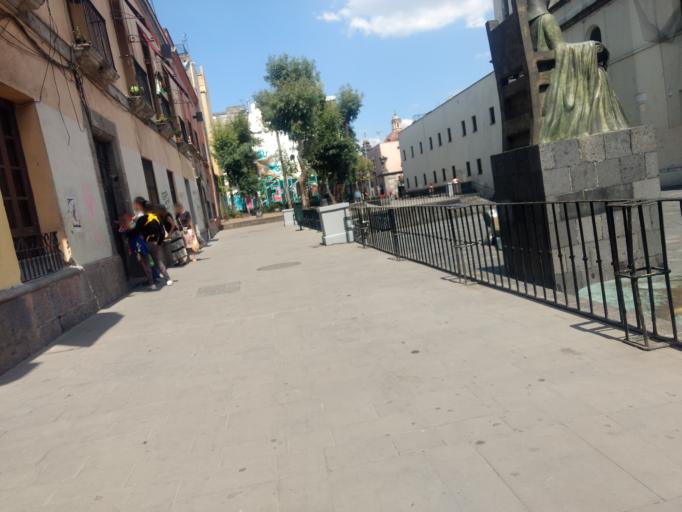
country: MX
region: Mexico City
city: Mexico City
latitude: 19.4270
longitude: -99.1359
